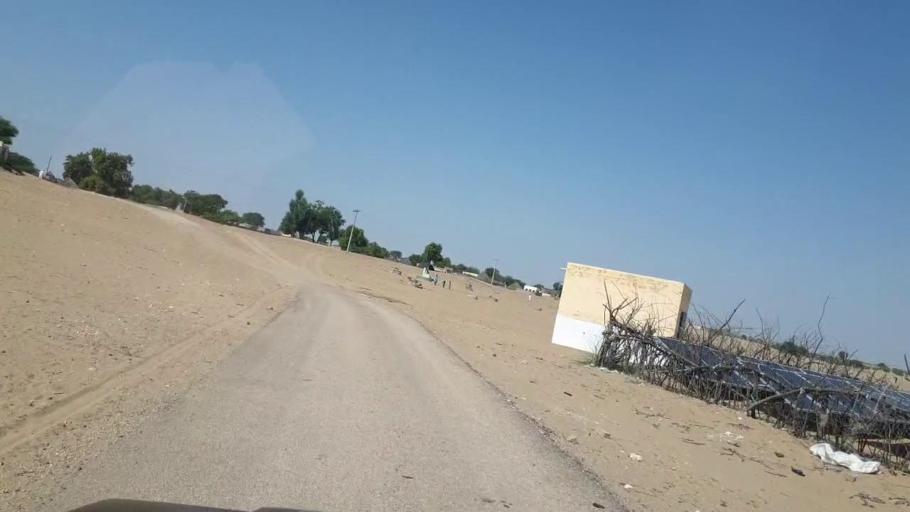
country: PK
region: Sindh
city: Chor
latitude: 25.6465
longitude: 70.3211
